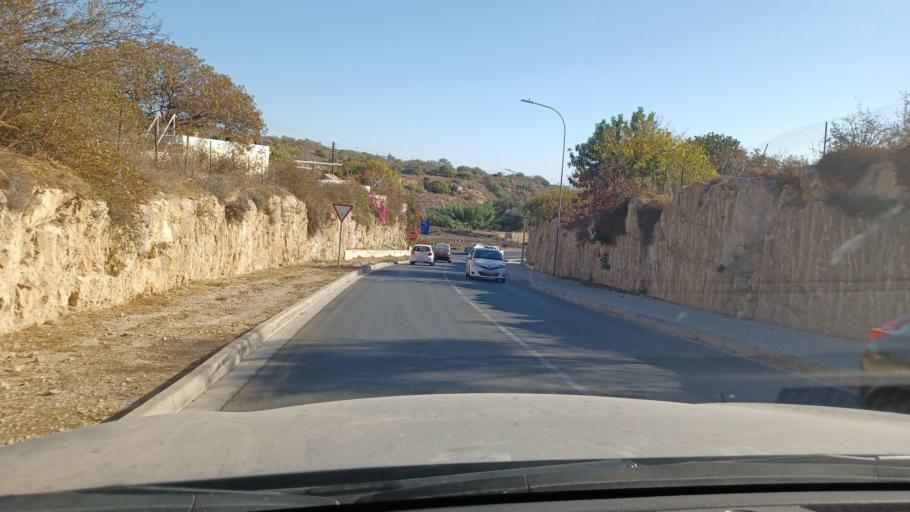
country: CY
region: Pafos
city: Paphos
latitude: 34.7864
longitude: 32.4463
